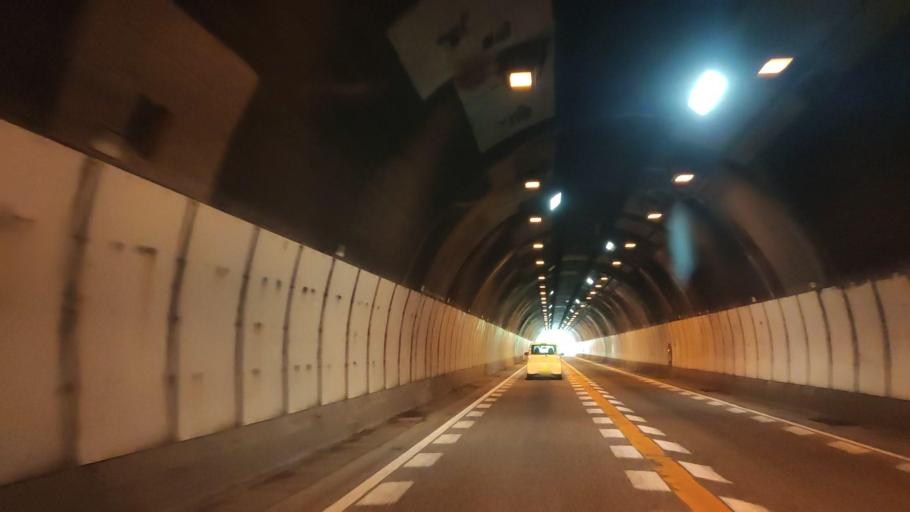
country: JP
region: Hyogo
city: Toyooka
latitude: 35.4848
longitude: 134.5777
